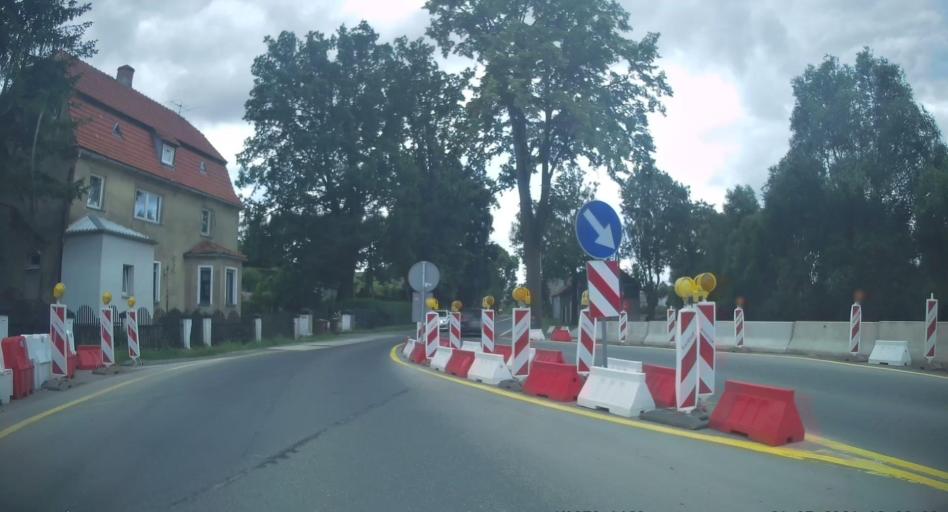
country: PL
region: Lower Silesian Voivodeship
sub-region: Powiat kamiennogorski
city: Kamienna Gora
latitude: 50.7942
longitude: 16.0403
